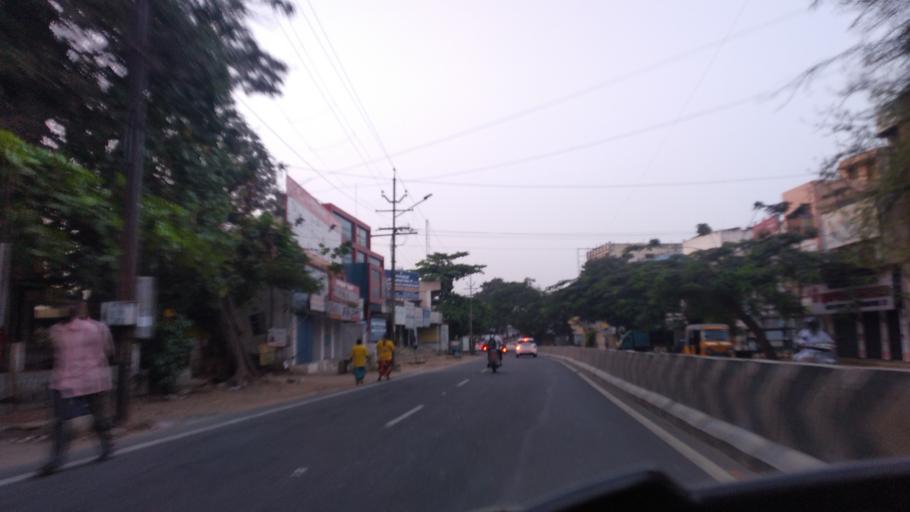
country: IN
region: Tamil Nadu
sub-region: Coimbatore
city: Coimbatore
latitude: 11.0051
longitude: 76.9665
